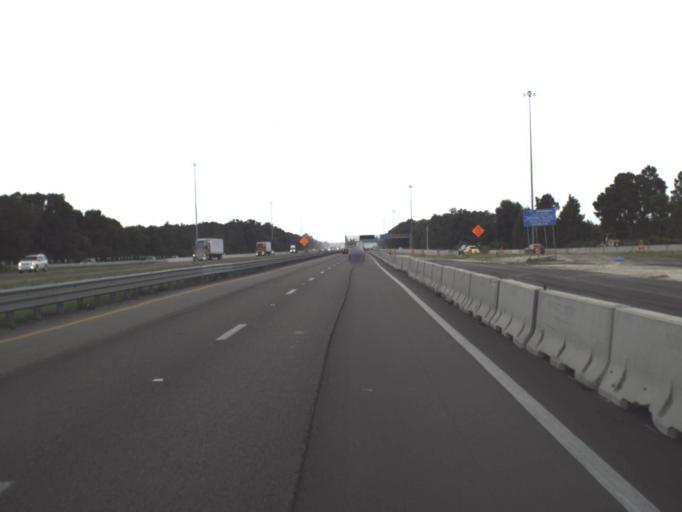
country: US
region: Florida
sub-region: Hillsborough County
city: Pebble Creek
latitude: 28.1922
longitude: -82.3851
